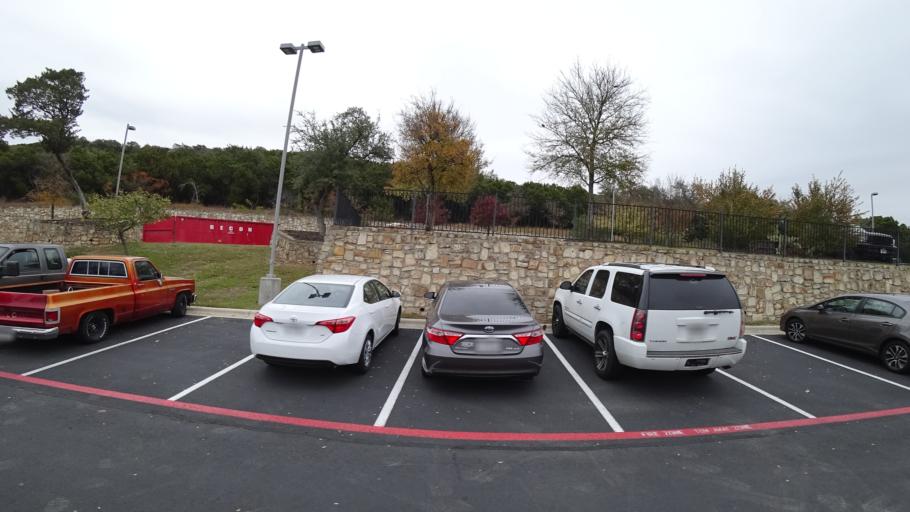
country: US
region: Texas
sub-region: Travis County
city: West Lake Hills
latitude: 30.3716
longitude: -97.8009
